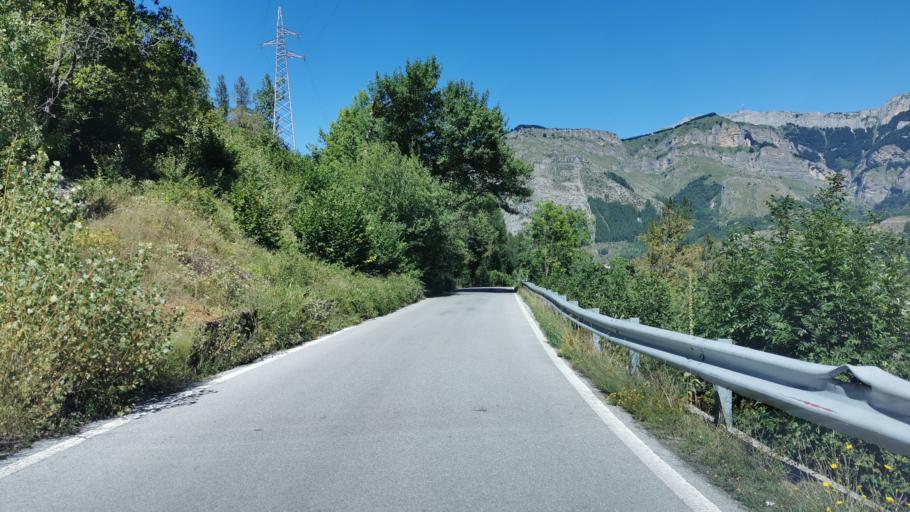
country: IT
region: Piedmont
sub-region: Provincia di Cuneo
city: Entracque
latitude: 44.2255
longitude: 7.3877
